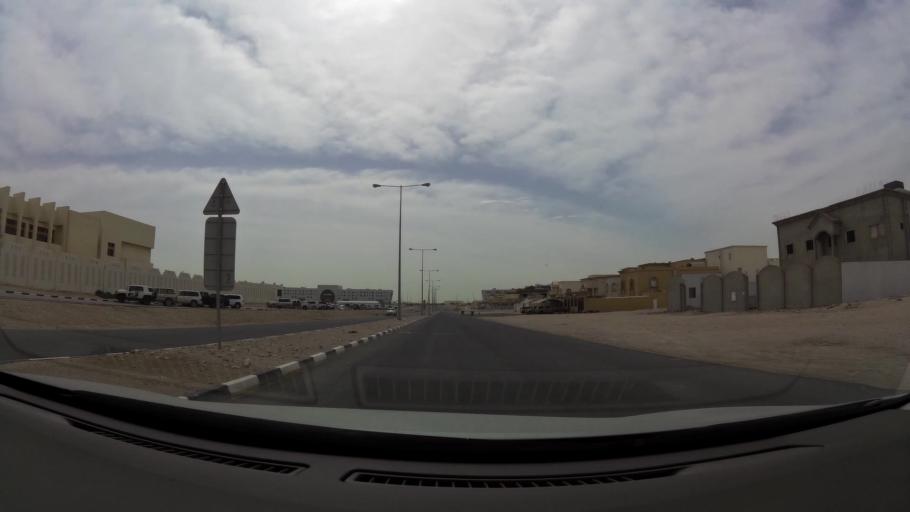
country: QA
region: Baladiyat ad Dawhah
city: Doha
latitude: 25.2155
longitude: 51.4926
